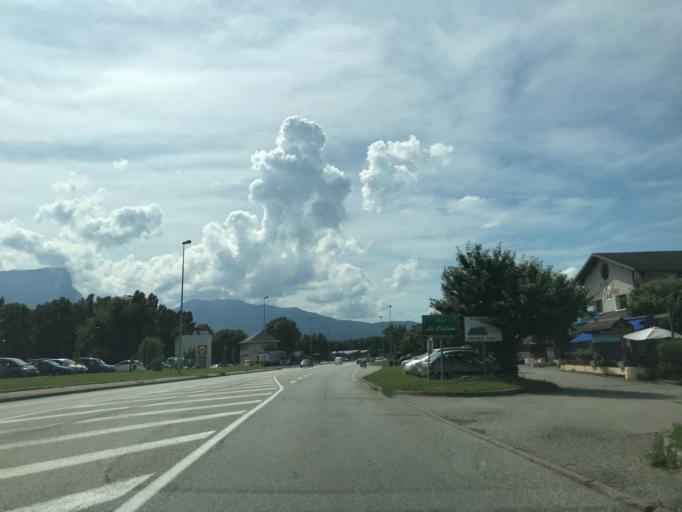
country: FR
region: Rhone-Alpes
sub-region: Departement de la Savoie
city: Montmelian
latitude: 45.4966
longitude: 6.0520
